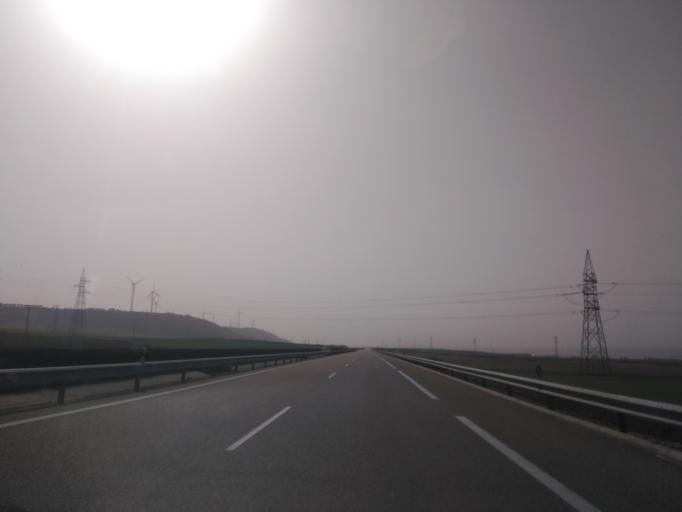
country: ES
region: Castille and Leon
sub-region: Provincia de Palencia
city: Villalobon
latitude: 42.0193
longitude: -4.4943
